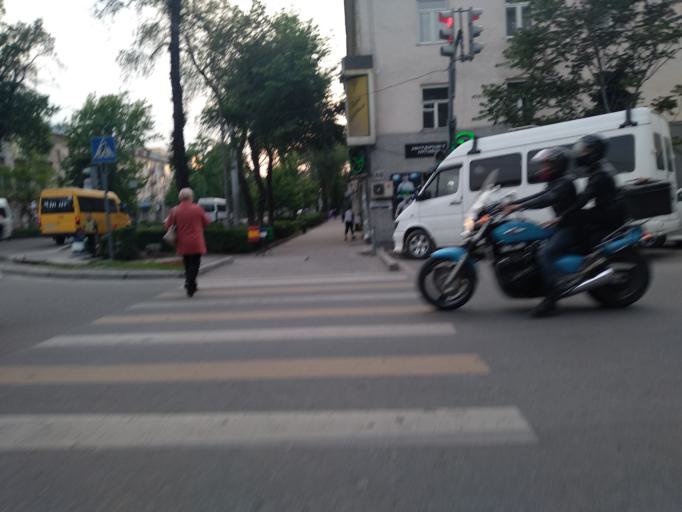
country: KG
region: Chuy
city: Bishkek
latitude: 42.8769
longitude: 74.5850
